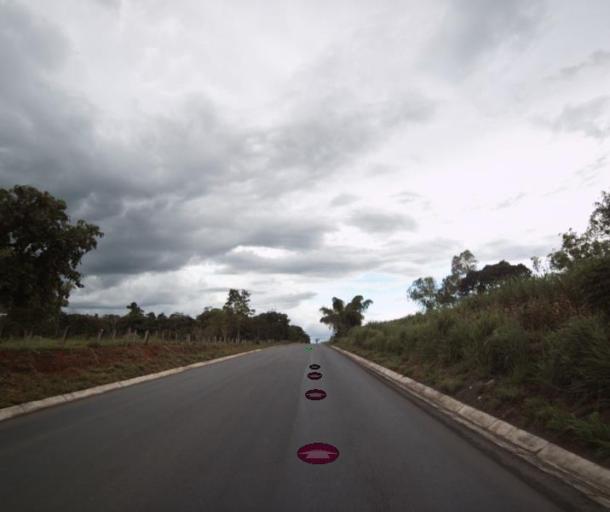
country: BR
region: Goias
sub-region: Itapaci
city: Itapaci
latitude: -14.9976
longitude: -49.4092
